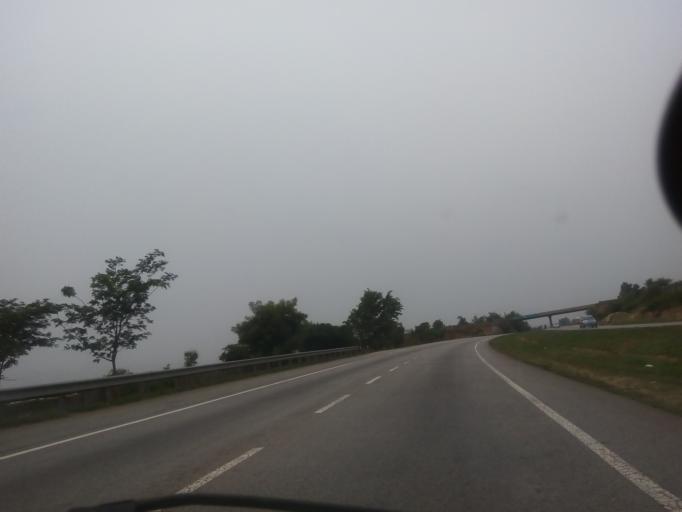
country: IN
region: Karnataka
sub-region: Bangalore Urban
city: Bangalore
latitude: 12.9122
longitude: 77.4673
